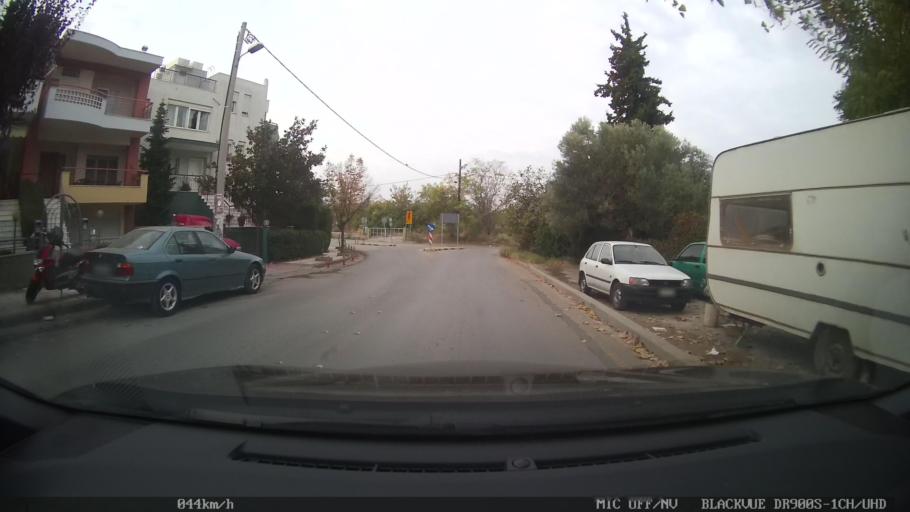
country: GR
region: Central Macedonia
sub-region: Nomos Thessalonikis
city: Pylaia
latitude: 40.5932
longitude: 22.9725
